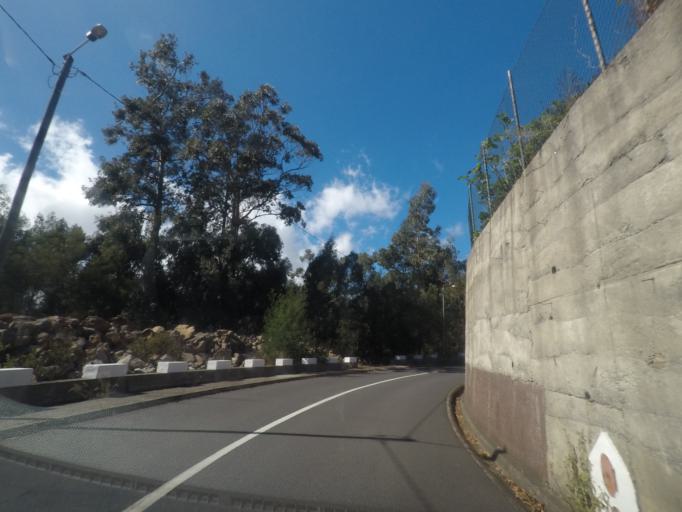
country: PT
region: Madeira
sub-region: Ribeira Brava
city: Campanario
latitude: 32.6825
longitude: -17.0417
